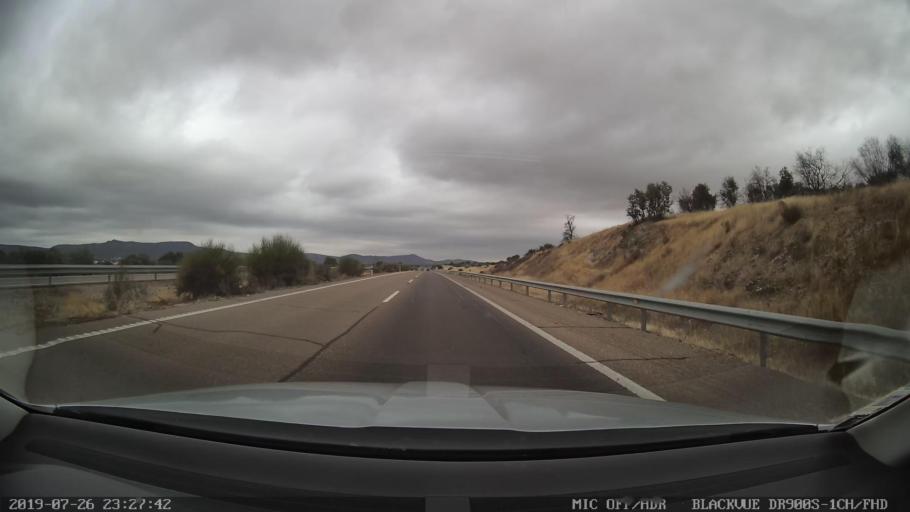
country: ES
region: Extremadura
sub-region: Provincia de Caceres
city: Villamesias
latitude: 39.2319
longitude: -5.8831
